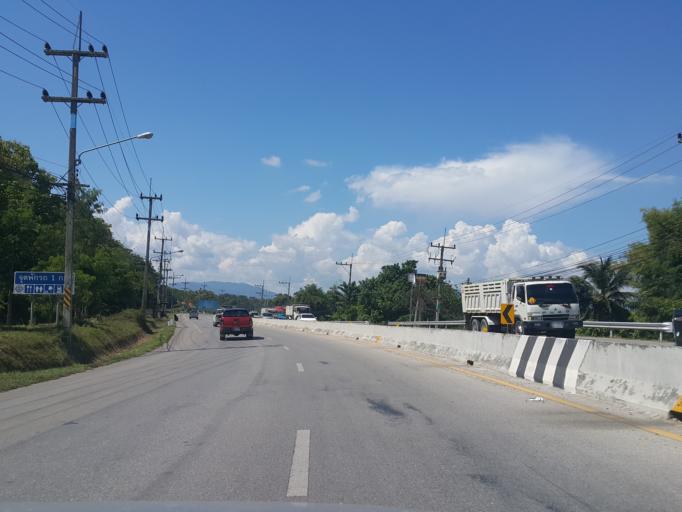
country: TH
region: Chiang Mai
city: Mae Taeng
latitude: 19.0498
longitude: 98.9467
